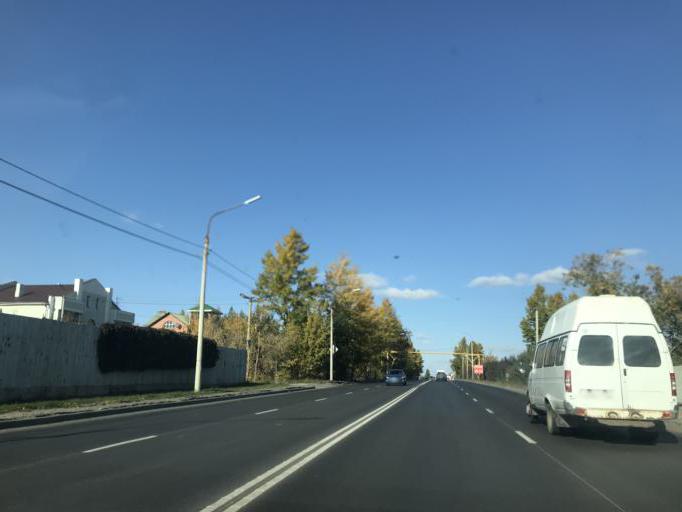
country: RU
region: Chelyabinsk
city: Roshchino
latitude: 55.2370
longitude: 61.3175
